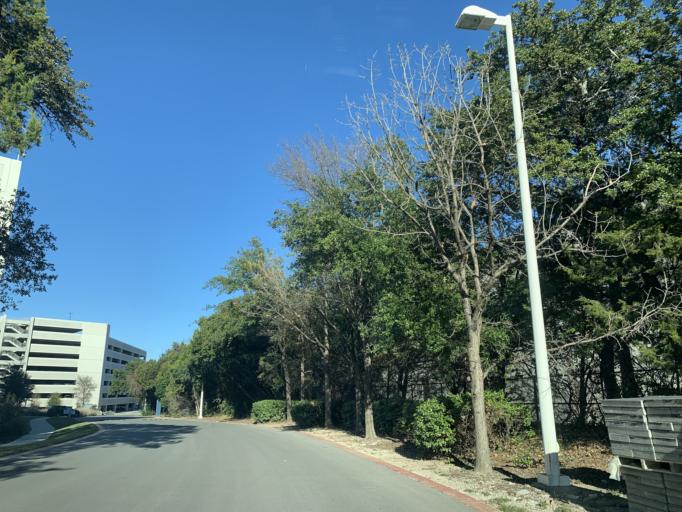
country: US
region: Texas
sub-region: Travis County
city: Wells Branch
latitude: 30.3976
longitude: -97.7114
